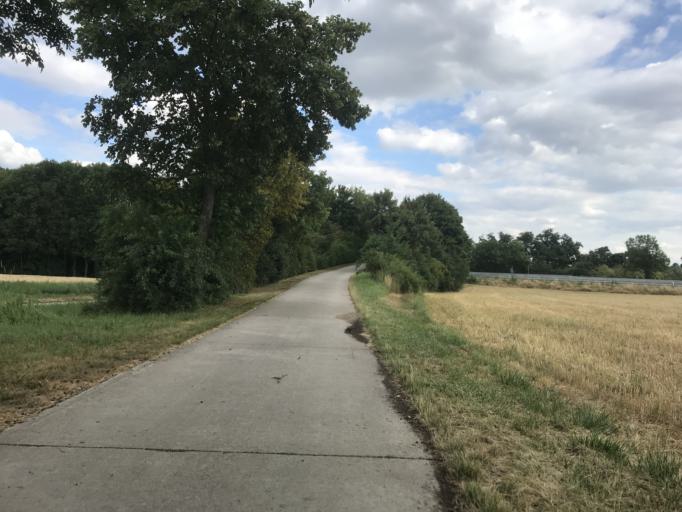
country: DE
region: Hesse
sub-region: Regierungsbezirk Darmstadt
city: Hochheim am Main
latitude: 50.0240
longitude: 8.3347
